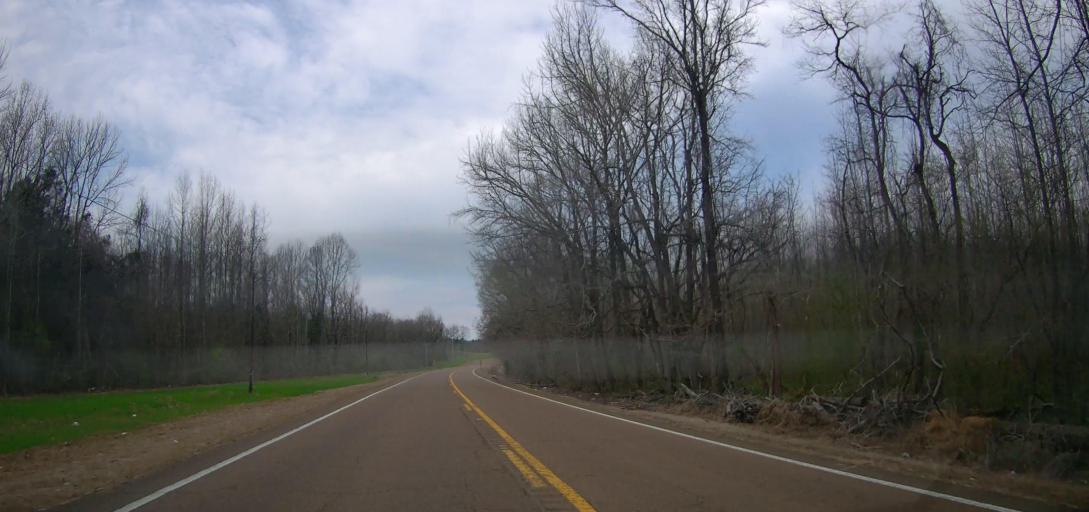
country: US
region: Mississippi
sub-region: Marshall County
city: Byhalia
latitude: 34.8481
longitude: -89.6253
